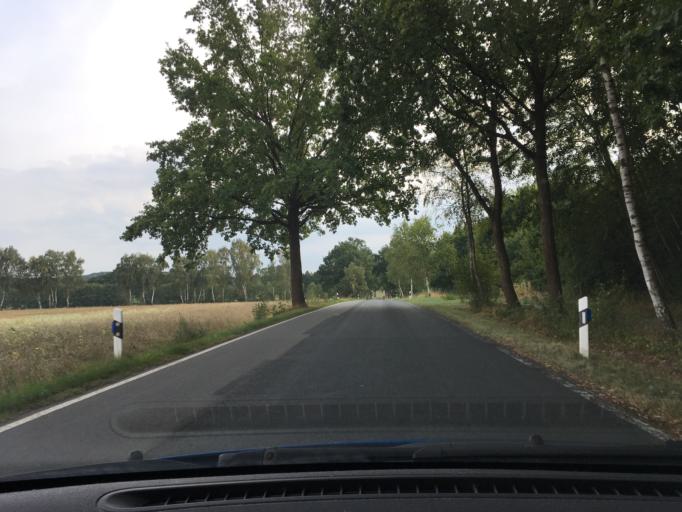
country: DE
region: Lower Saxony
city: Asendorf
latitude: 53.2767
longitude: 9.9736
